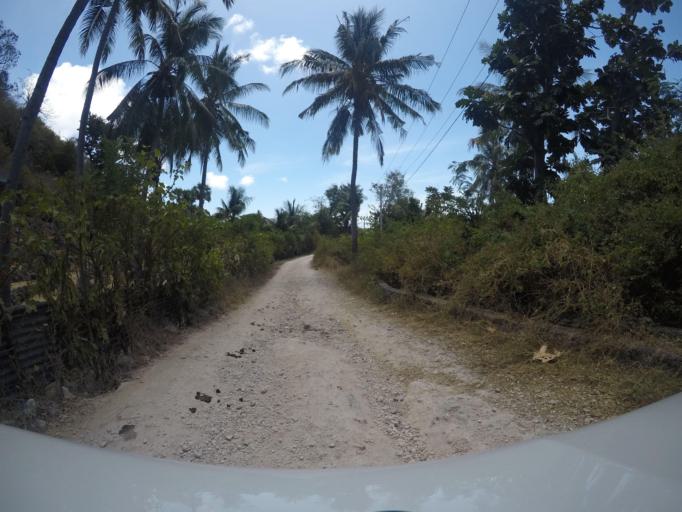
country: TL
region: Baucau
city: Baucau
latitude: -8.4520
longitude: 126.4411
